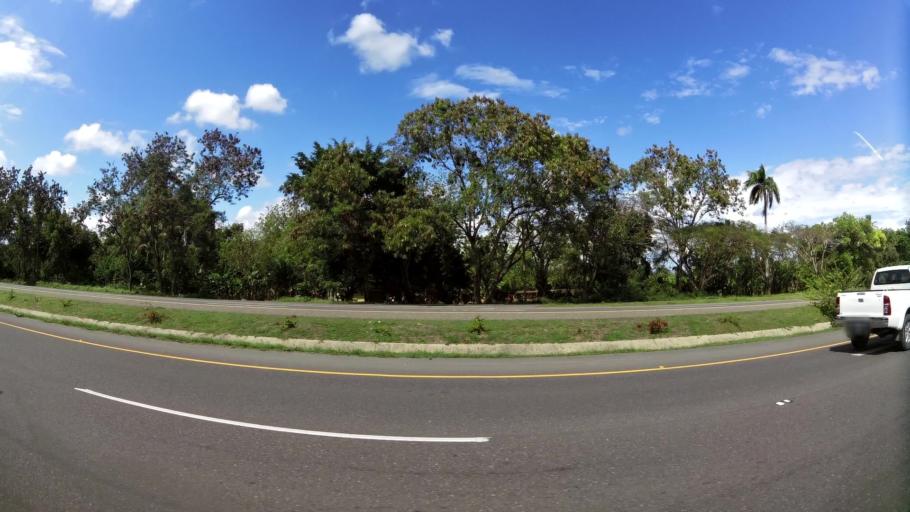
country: DO
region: La Vega
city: Concepcion de La Vega
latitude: 19.2463
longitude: -70.5433
